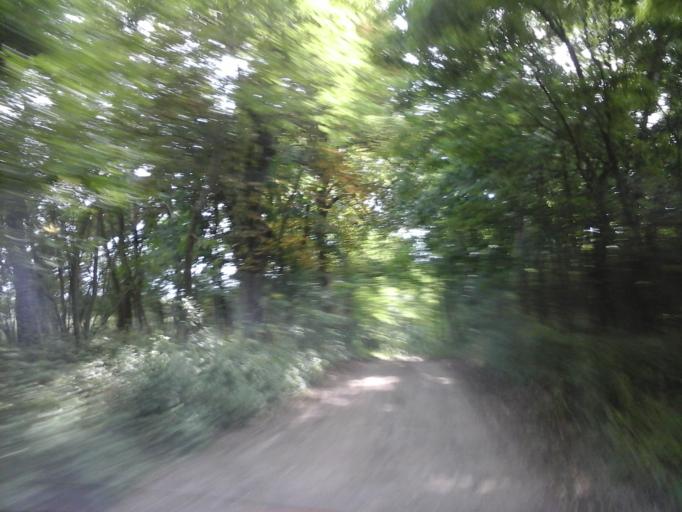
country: PL
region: West Pomeranian Voivodeship
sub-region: Powiat choszczenski
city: Recz
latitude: 53.2440
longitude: 15.6136
